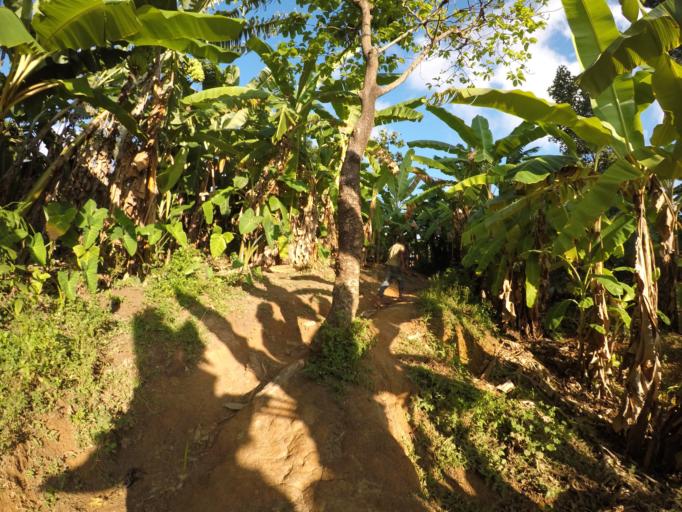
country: TZ
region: Pemba South
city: Mtambile
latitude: -5.3886
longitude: 39.7458
